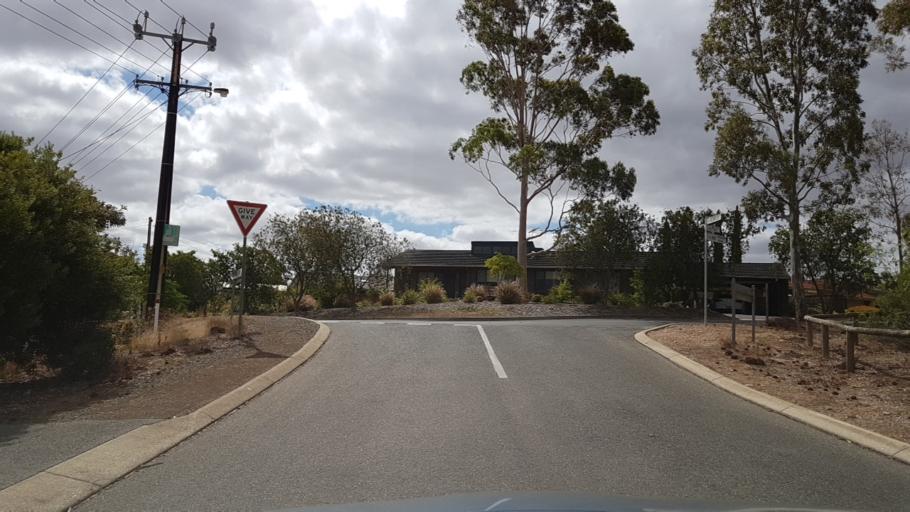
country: AU
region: South Australia
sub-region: Gawler
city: Gawler
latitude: -34.6100
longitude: 138.7546
